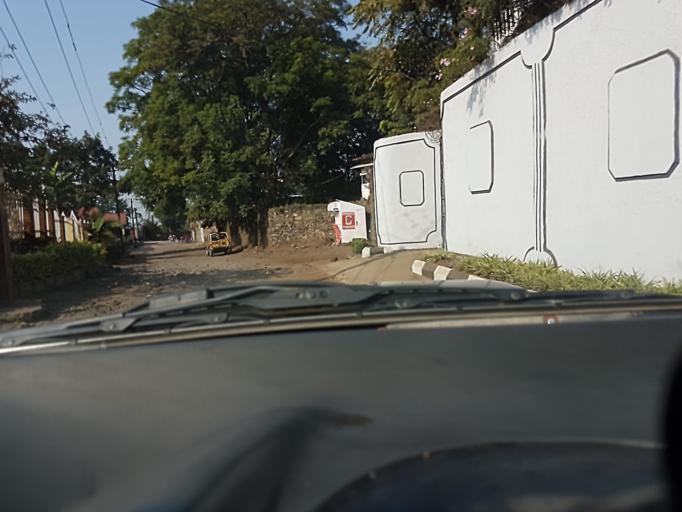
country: RW
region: Western Province
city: Gisenyi
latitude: -1.6965
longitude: 29.2392
